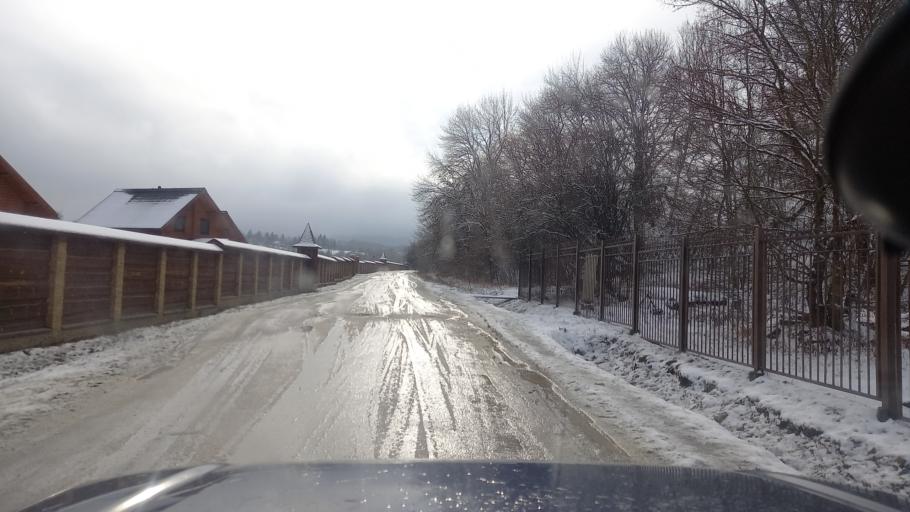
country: RU
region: Adygeya
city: Kamennomostskiy
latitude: 44.2357
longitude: 40.1924
